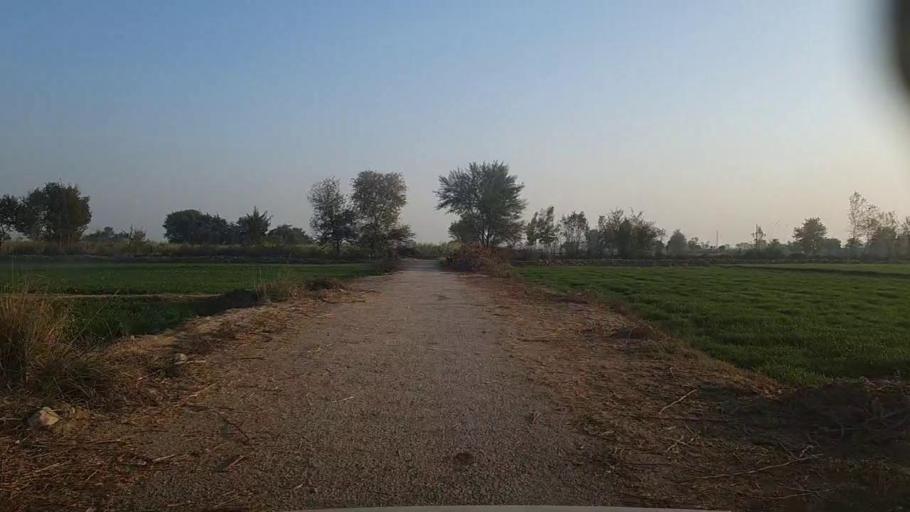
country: PK
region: Sindh
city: Khairpur
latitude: 28.0572
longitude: 69.7581
